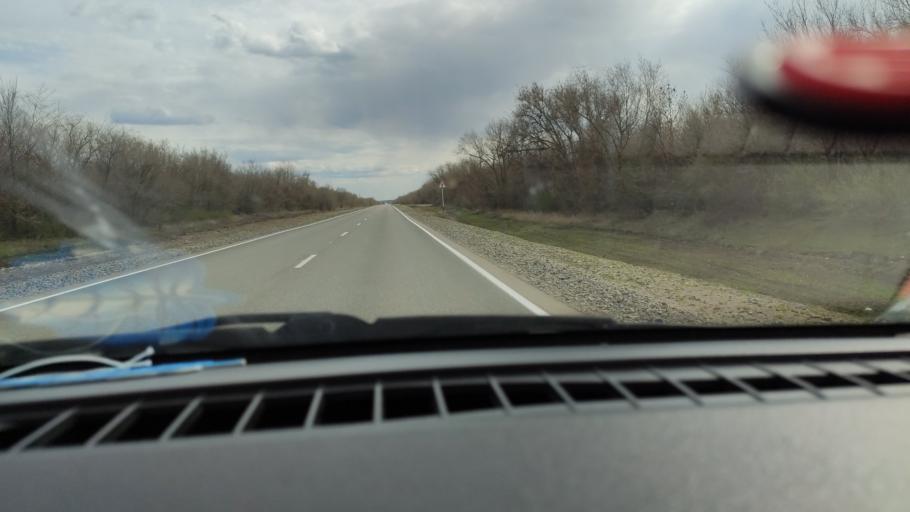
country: RU
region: Saratov
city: Privolzhskiy
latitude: 51.1418
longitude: 45.9600
